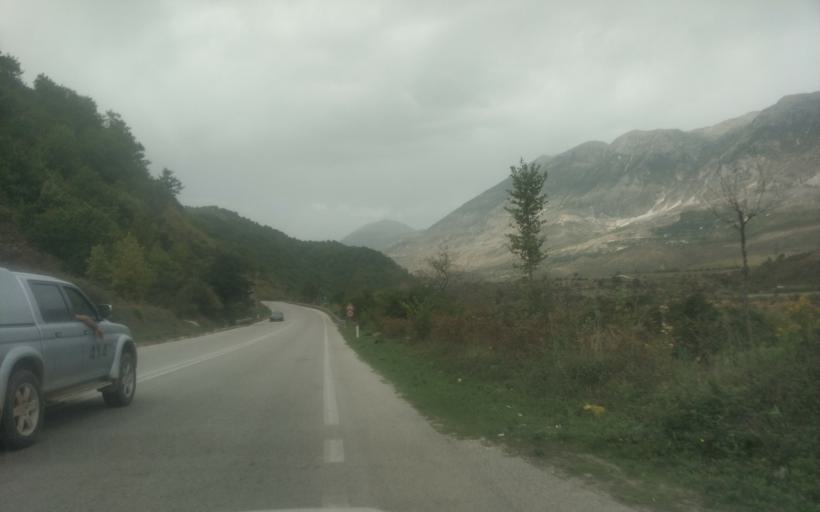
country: AL
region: Gjirokaster
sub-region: Rrethi i Gjirokastres
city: Picar
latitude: 40.2114
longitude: 20.0882
